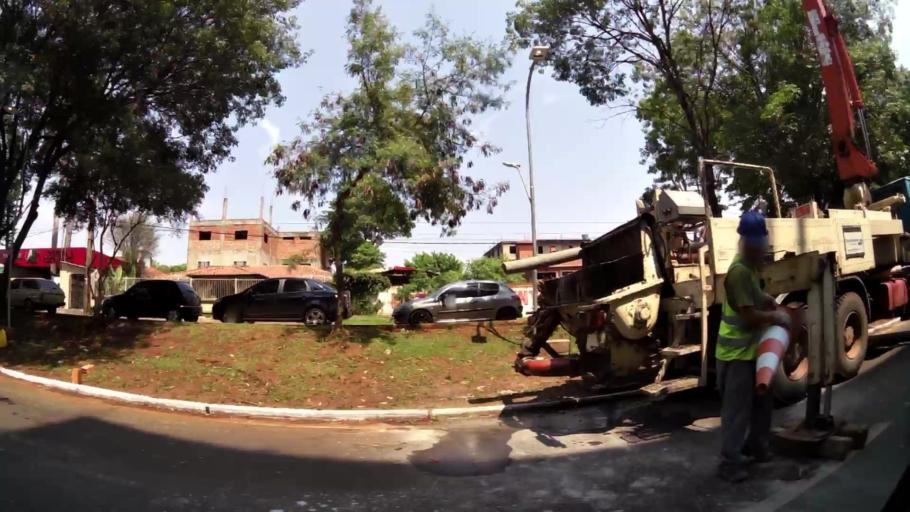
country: PY
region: Alto Parana
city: Presidente Franco
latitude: -25.5229
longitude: -54.6104
